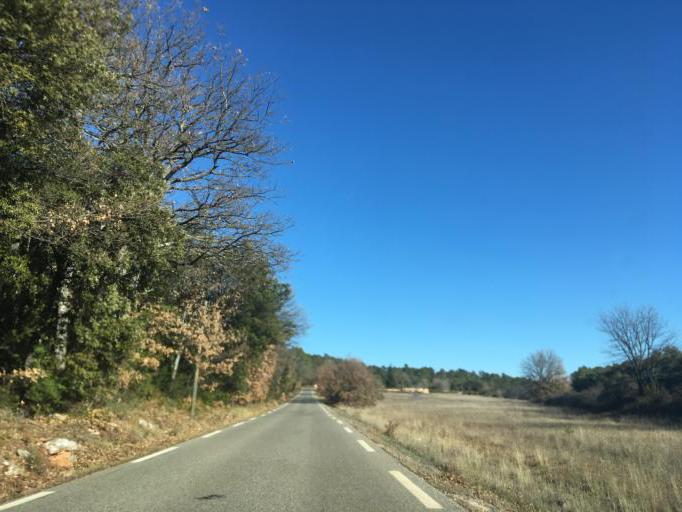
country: FR
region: Provence-Alpes-Cote d'Azur
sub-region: Departement du Var
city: Barjols
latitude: 43.5935
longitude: 6.0566
